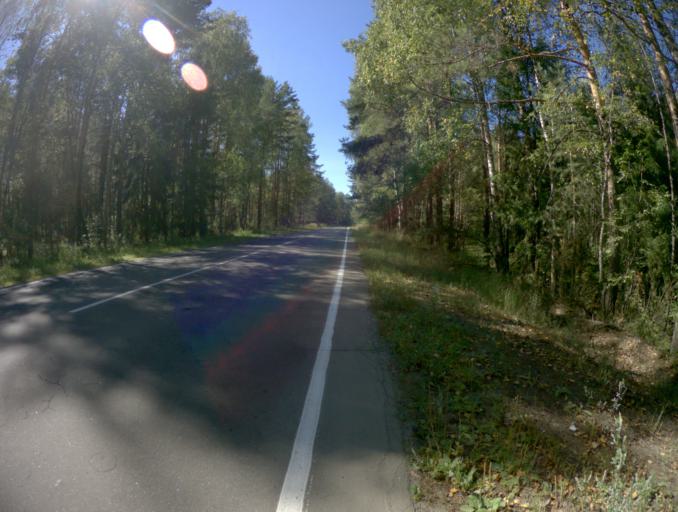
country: RU
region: Vladimir
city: Zolotkovo
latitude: 55.6184
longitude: 40.9853
